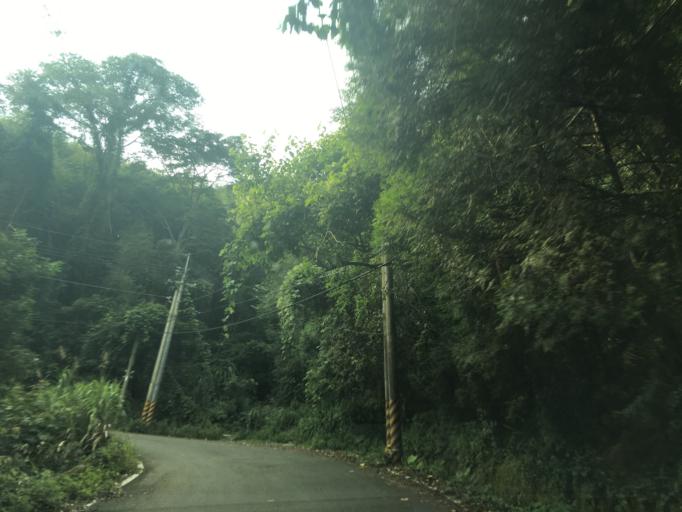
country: TW
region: Taiwan
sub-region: Miaoli
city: Miaoli
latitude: 24.3977
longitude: 120.9787
